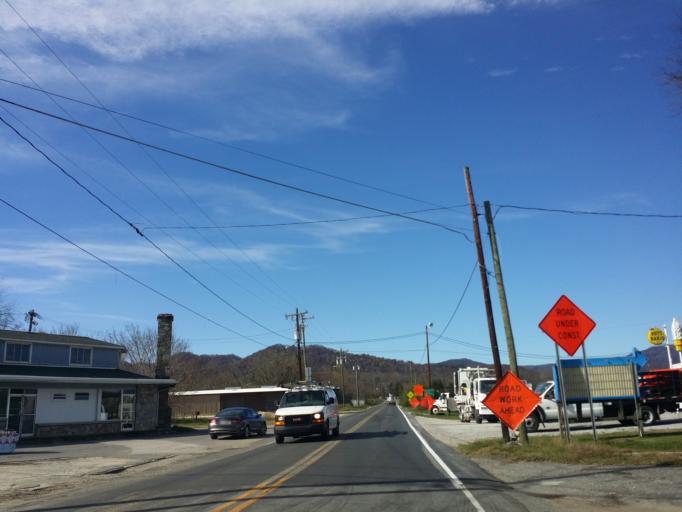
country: US
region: North Carolina
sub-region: McDowell County
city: West Marion
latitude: 35.6923
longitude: -82.0620
